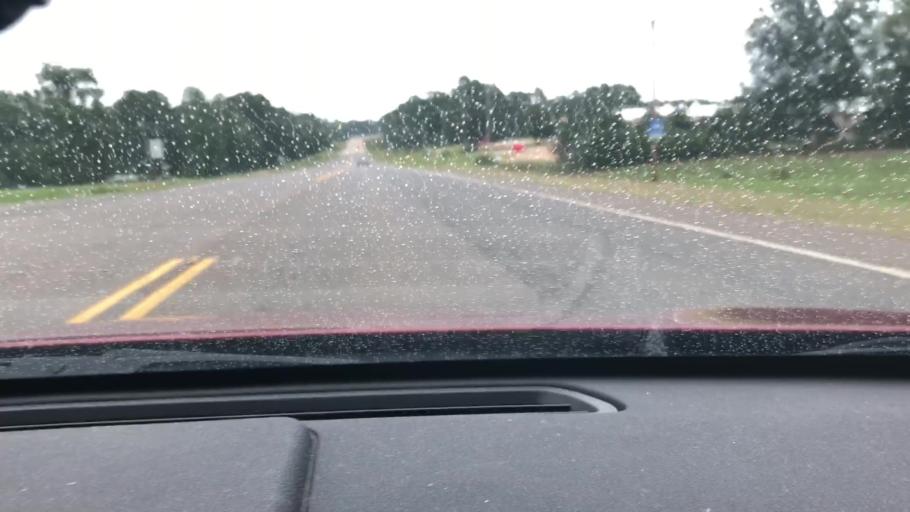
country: US
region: Arkansas
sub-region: Lafayette County
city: Lewisville
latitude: 33.3594
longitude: -93.5564
